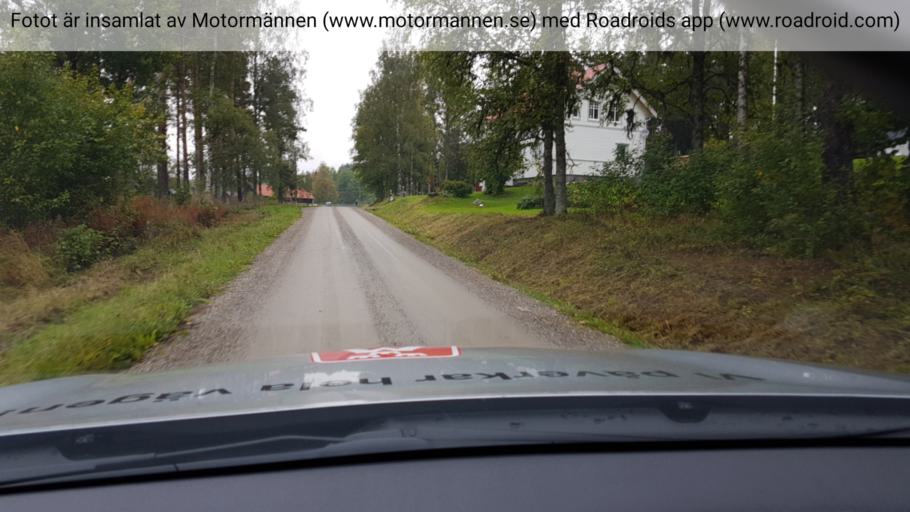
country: SE
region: Jaemtland
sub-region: Braecke Kommun
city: Braecke
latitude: 62.7602
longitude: 15.4995
